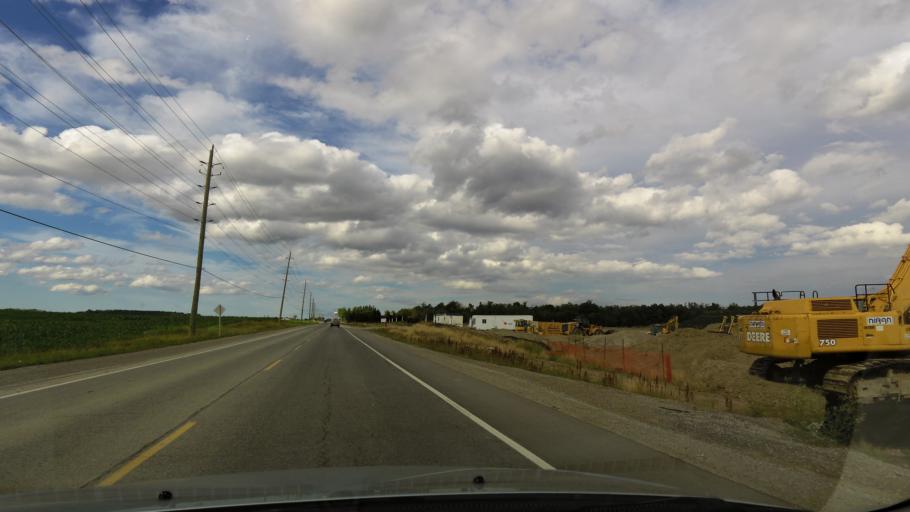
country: CA
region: Ontario
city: Brampton
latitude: 43.7159
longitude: -79.8441
